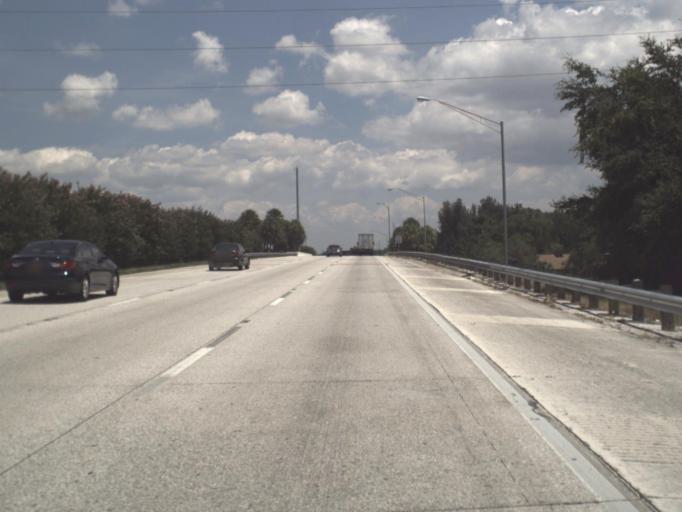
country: US
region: Florida
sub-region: Pinellas County
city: Gulfport
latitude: 27.7318
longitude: -82.6765
